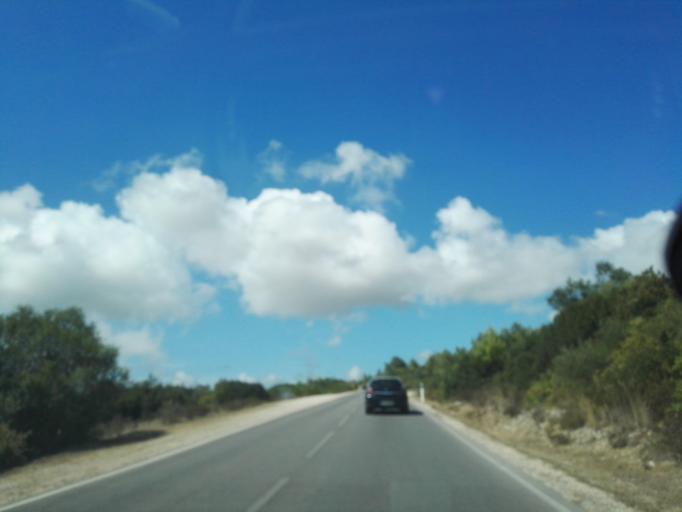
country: PT
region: Setubal
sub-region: Sesimbra
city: Sesimbra
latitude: 38.4464
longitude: -9.0874
